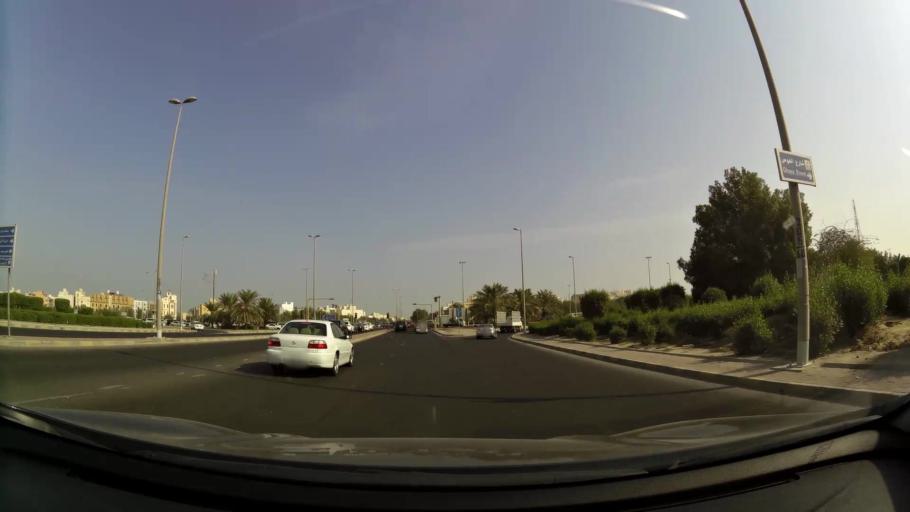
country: KW
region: Mubarak al Kabir
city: Mubarak al Kabir
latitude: 29.1967
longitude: 48.0907
